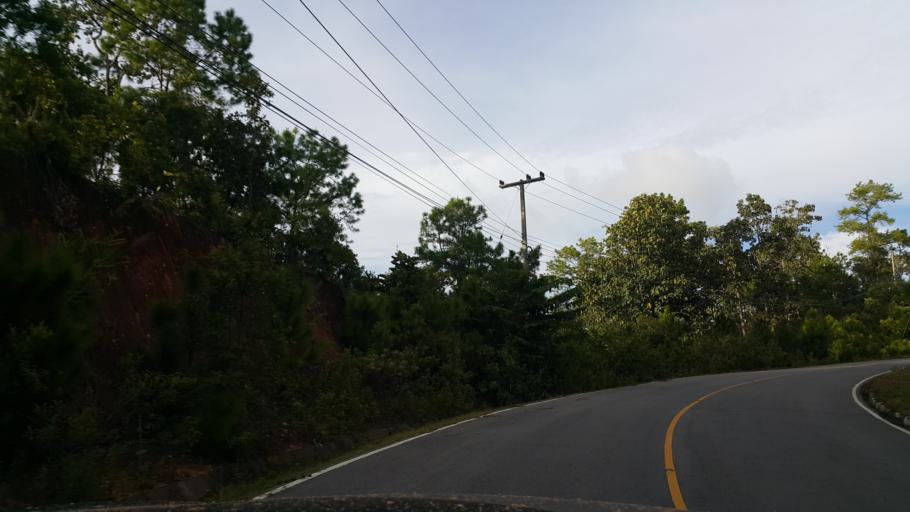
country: TH
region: Chiang Mai
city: Chaem Luang
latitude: 19.0996
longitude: 98.3474
